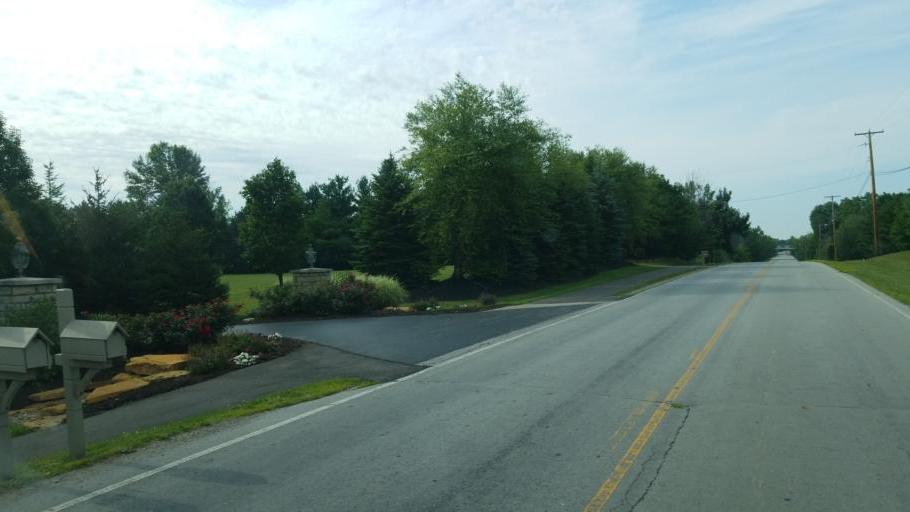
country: US
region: Ohio
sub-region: Franklin County
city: Dublin
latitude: 40.1578
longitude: -83.1535
